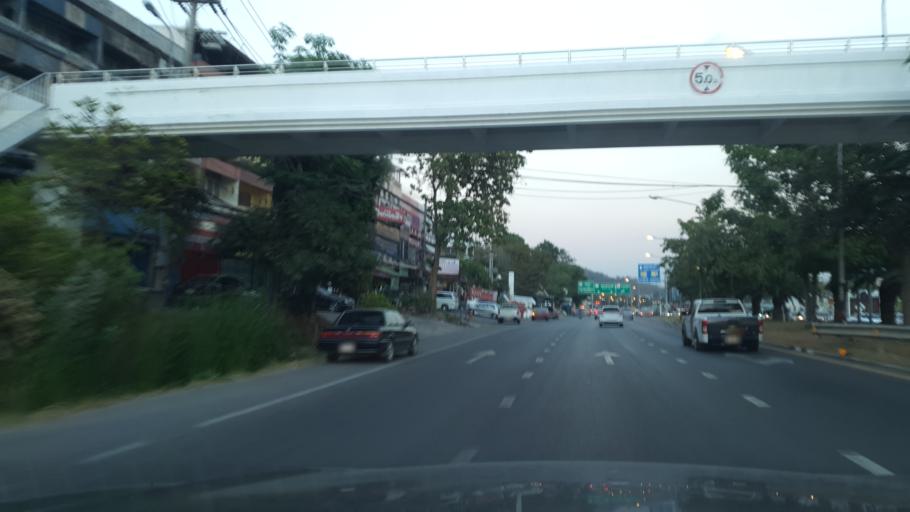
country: TH
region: Nakhon Sawan
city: Nakhon Sawan
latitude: 15.7086
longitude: 100.1144
